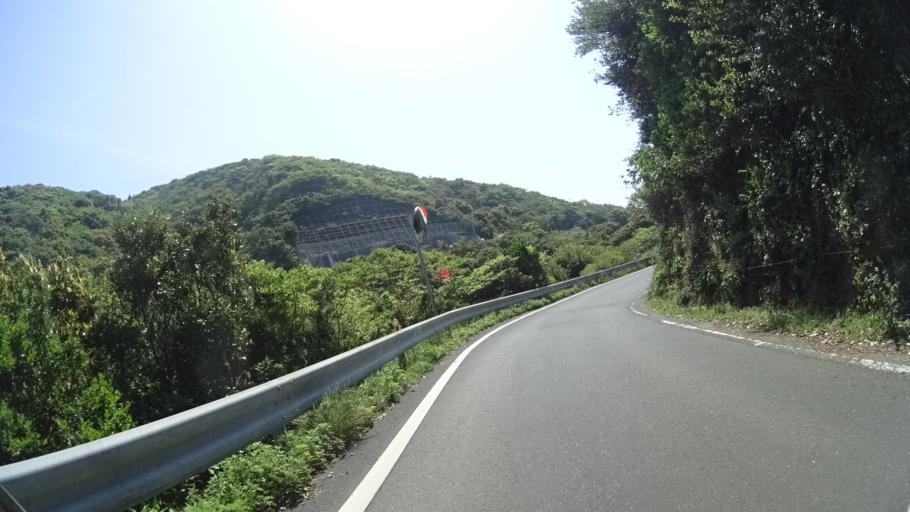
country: JP
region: Oita
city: Tsukumiura
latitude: 33.3558
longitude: 132.0375
